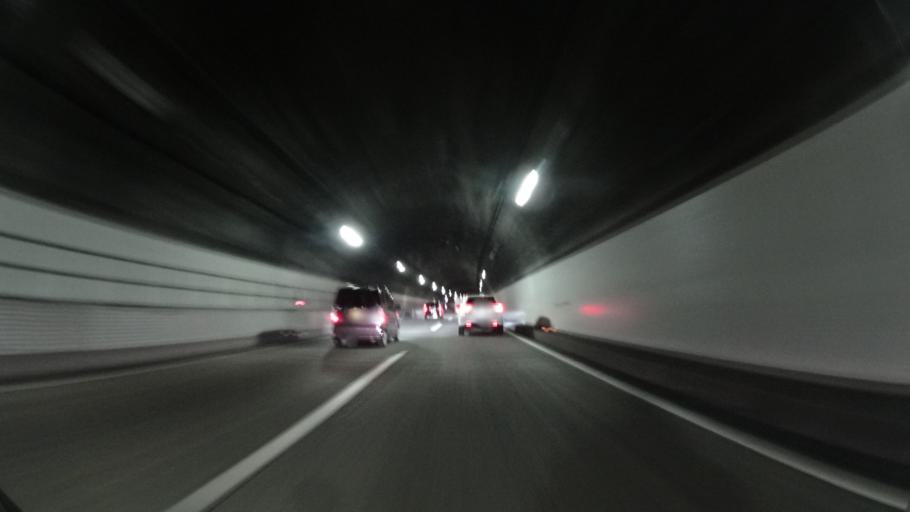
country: JP
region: Okayama
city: Okayama-shi
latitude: 34.7357
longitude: 133.9855
